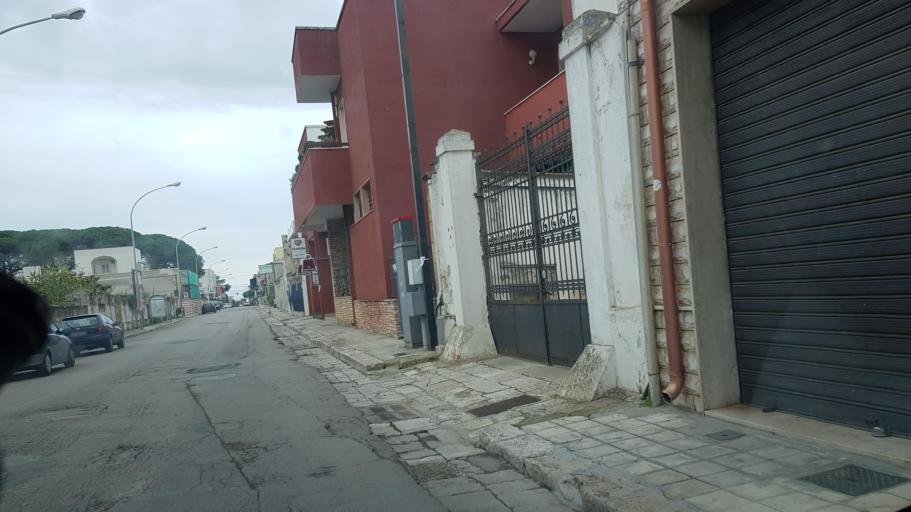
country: IT
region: Apulia
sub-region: Provincia di Lecce
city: Squinzano
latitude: 40.4374
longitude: 18.0388
